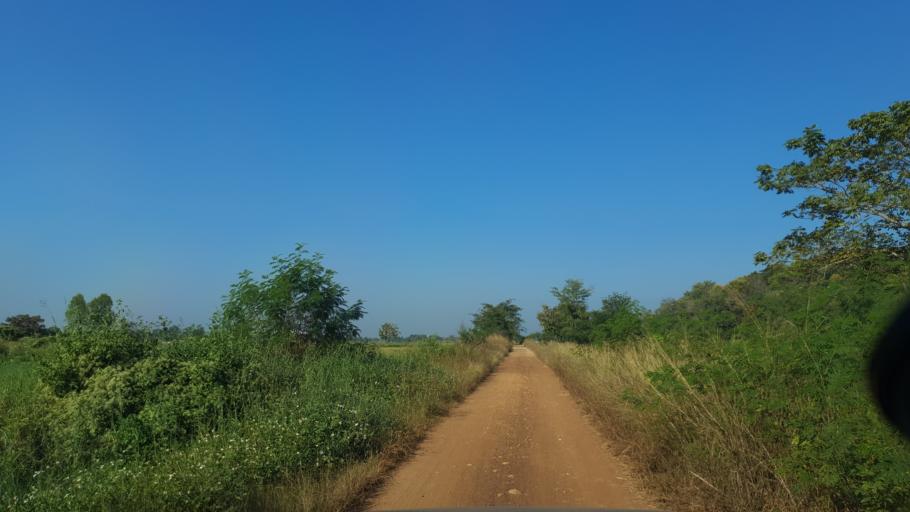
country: TH
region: Chiang Mai
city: San Kamphaeng
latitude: 18.7304
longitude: 99.1781
